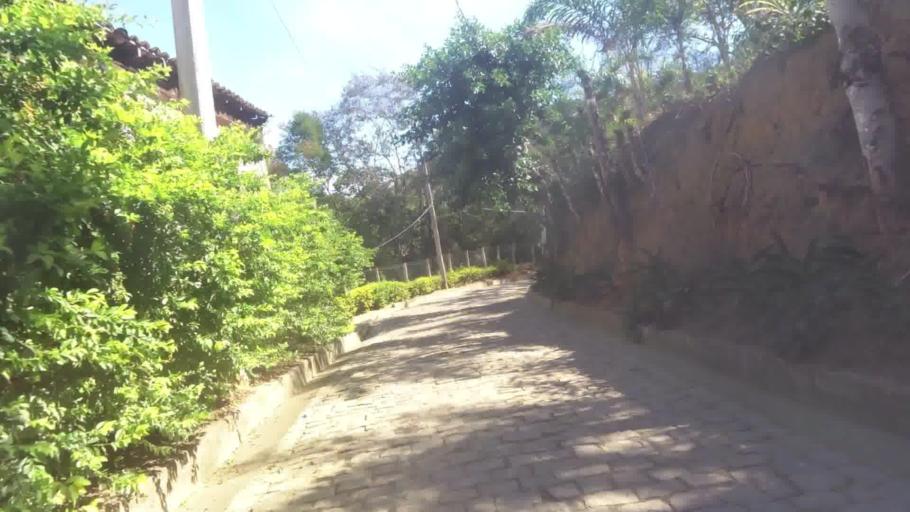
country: BR
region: Espirito Santo
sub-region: Vargem Alta
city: Vargem Alta
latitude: -20.6608
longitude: -41.0554
